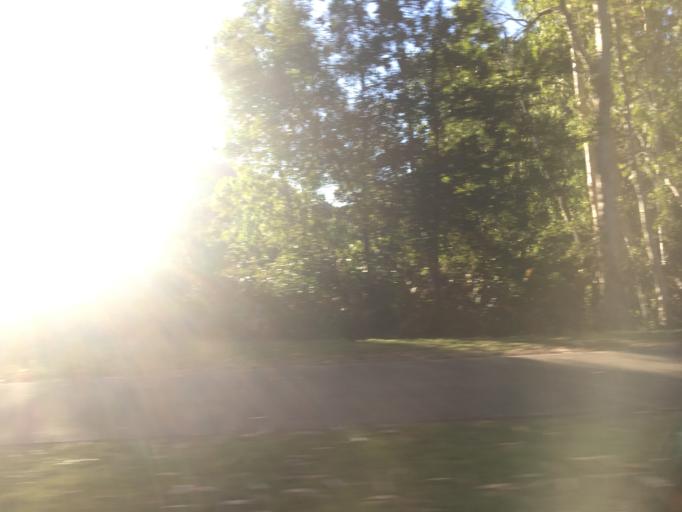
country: AU
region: Queensland
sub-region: Cairns
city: Yorkeys Knob
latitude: -16.8000
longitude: 145.7078
